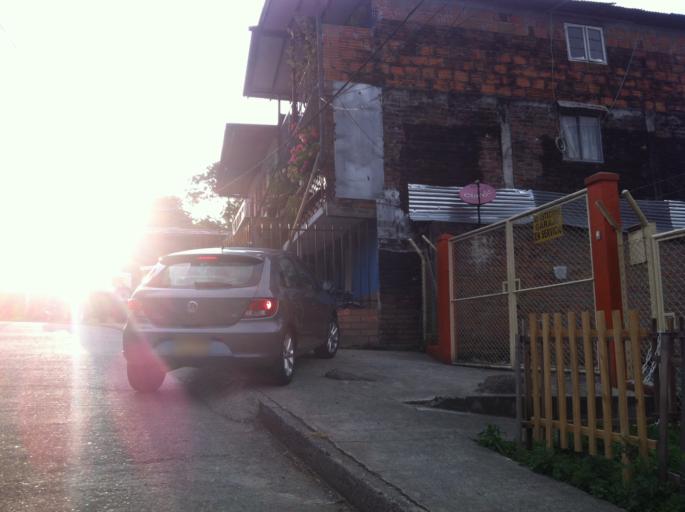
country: CO
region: Quindio
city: Filandia
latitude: 4.7596
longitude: -75.6115
